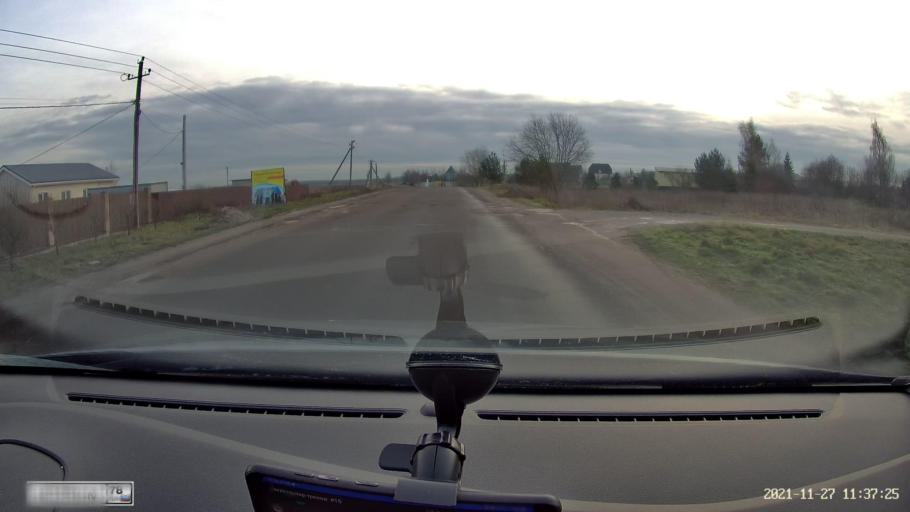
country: RU
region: Leningrad
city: Russko-Vysotskoye
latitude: 59.6942
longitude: 29.9872
